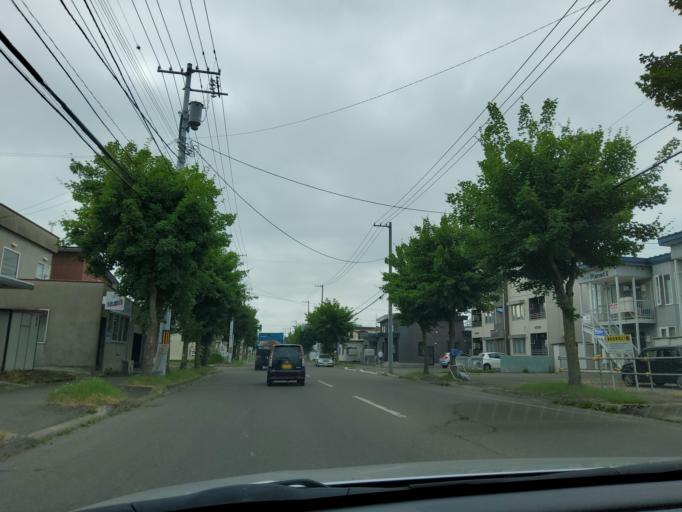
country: JP
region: Hokkaido
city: Obihiro
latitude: 42.9137
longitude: 143.1581
